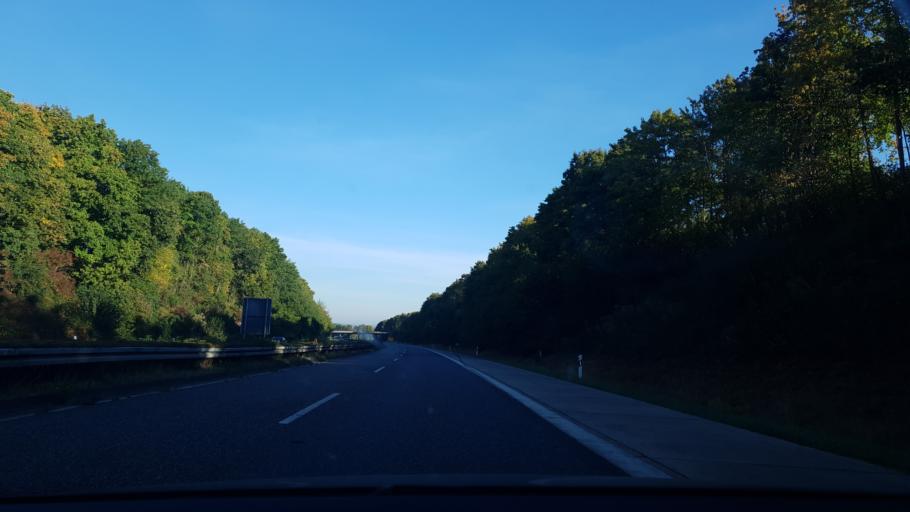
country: DE
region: Hesse
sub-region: Regierungsbezirk Giessen
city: Langgons
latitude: 50.4885
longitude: 8.6562
